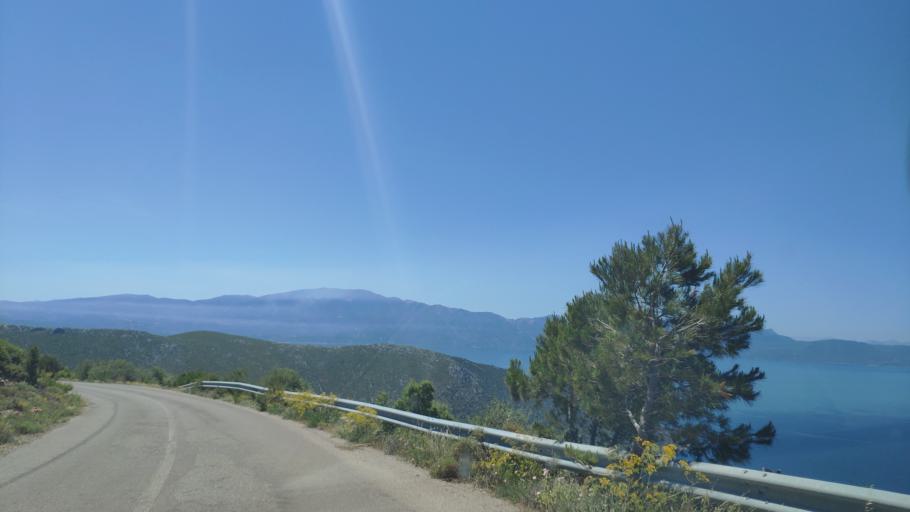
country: GR
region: Central Greece
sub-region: Nomos Voiotias
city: Kaparellion
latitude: 38.1964
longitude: 23.1460
